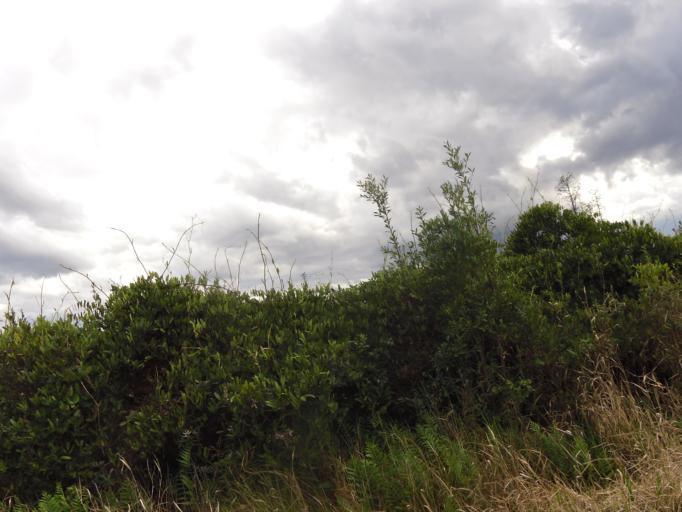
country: US
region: Georgia
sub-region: Charlton County
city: Folkston
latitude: 30.7129
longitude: -82.1674
